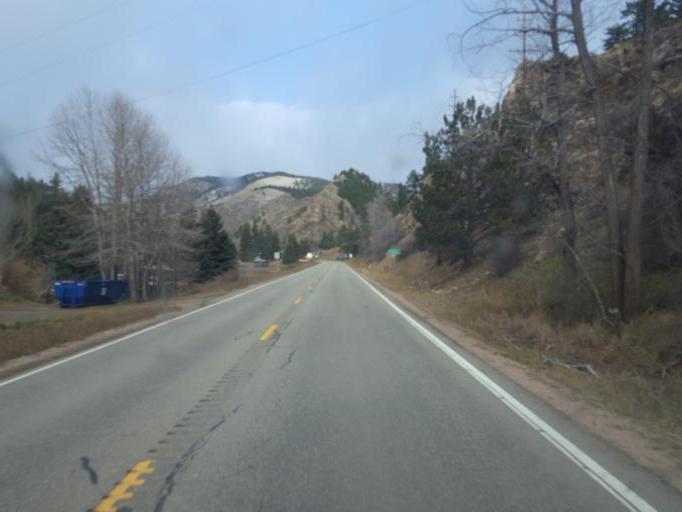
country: US
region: Colorado
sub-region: Clear Creek County
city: Georgetown
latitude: 39.4580
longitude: -105.6567
